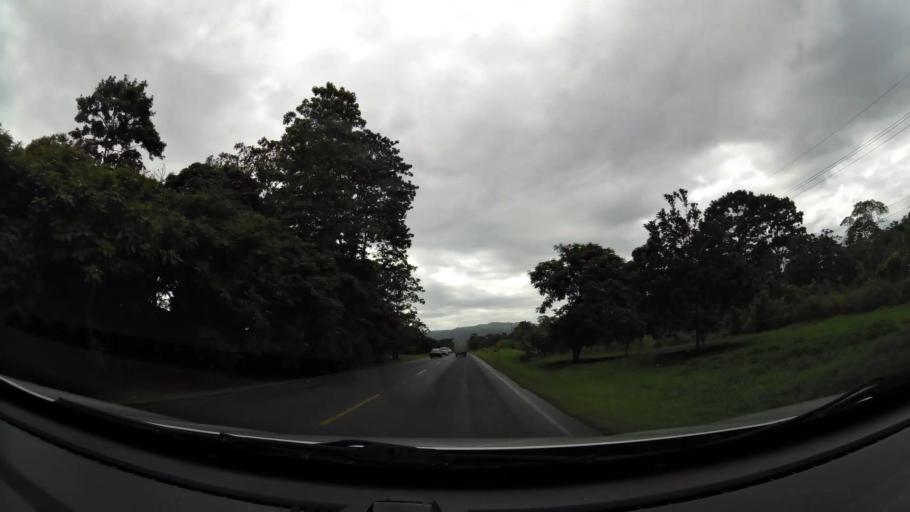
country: CR
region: Limon
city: Pocora
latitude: 10.1322
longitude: -83.5617
